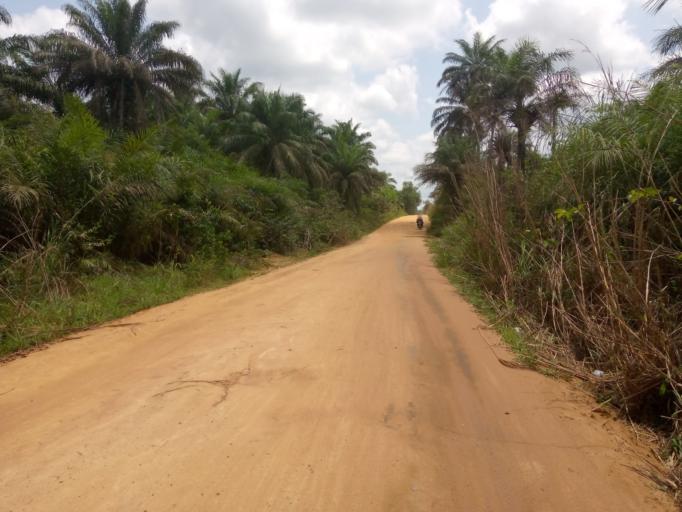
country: SL
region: Western Area
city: Waterloo
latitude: 8.3713
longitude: -12.9623
